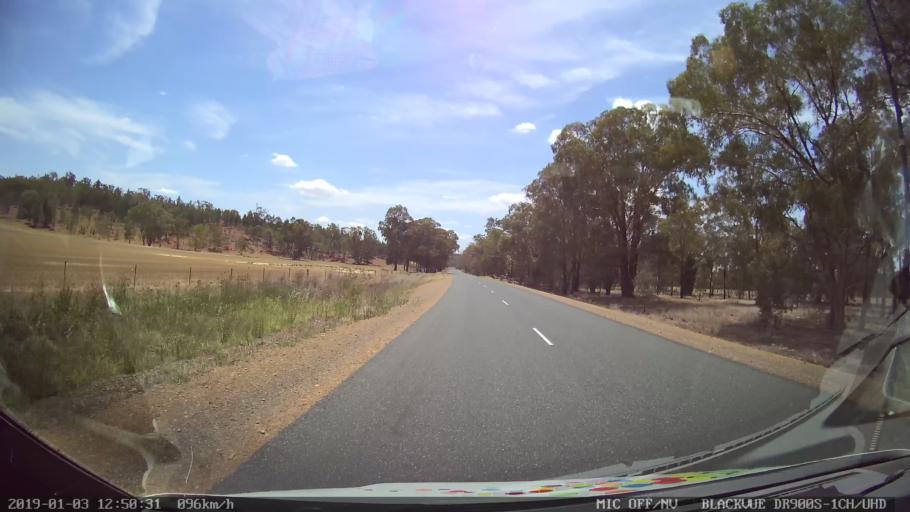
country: AU
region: New South Wales
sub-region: Weddin
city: Grenfell
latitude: -33.6906
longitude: 148.2714
